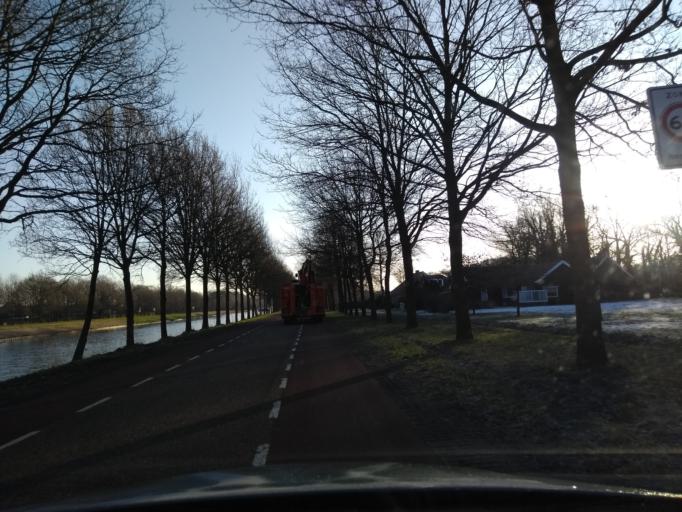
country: NL
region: Overijssel
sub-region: Gemeente Hof van Twente
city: Delden
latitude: 52.2519
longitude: 6.7059
